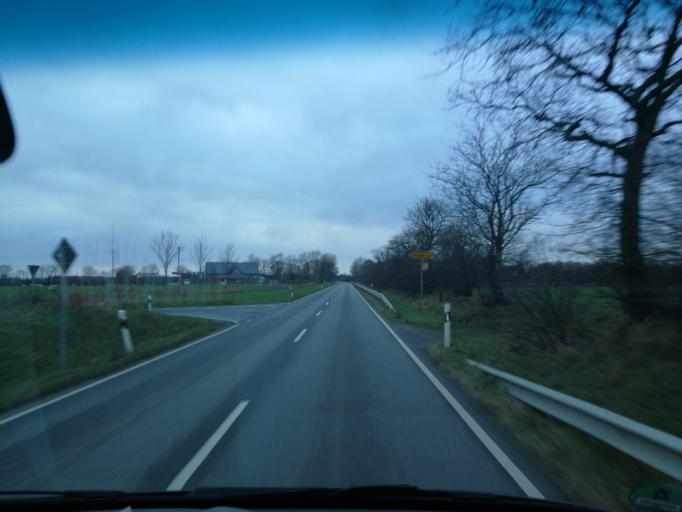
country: DE
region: Schleswig-Holstein
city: Wallsbull
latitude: 54.7989
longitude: 9.2764
